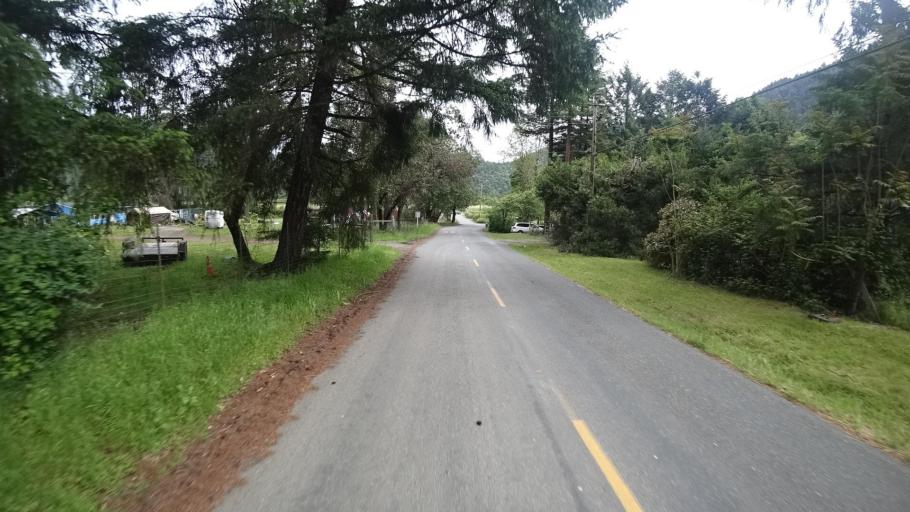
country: US
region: California
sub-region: Humboldt County
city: Willow Creek
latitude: 40.9716
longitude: -123.6304
